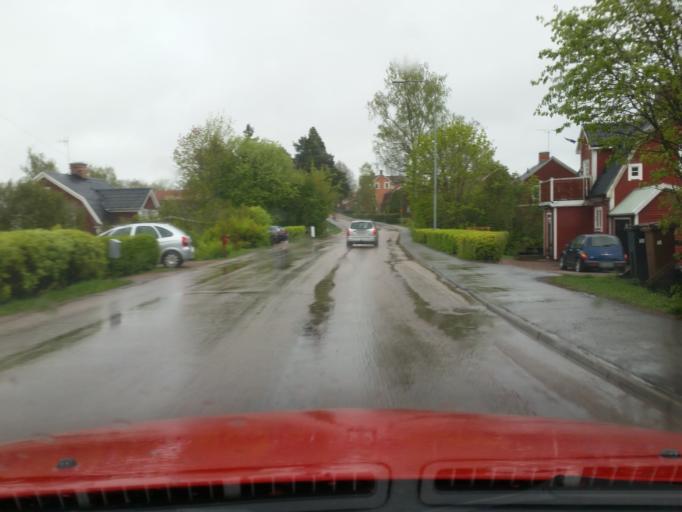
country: SE
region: Dalarna
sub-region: Hedemora Kommun
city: Hedemora
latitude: 60.2864
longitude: 15.9754
